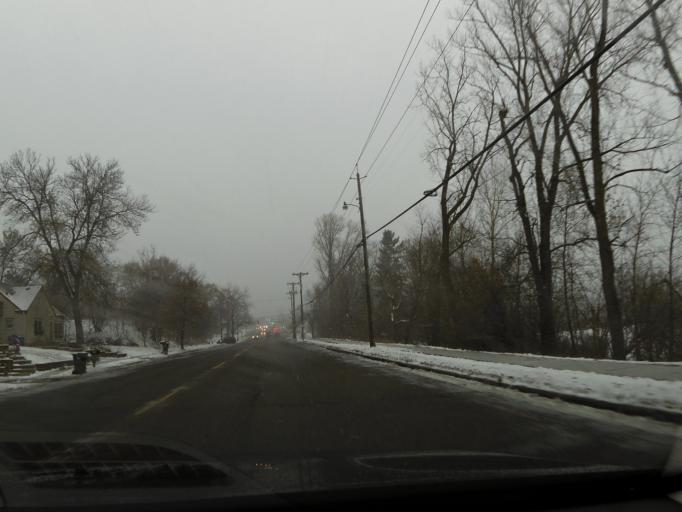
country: US
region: Minnesota
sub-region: Ramsey County
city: Maplewood
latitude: 44.9476
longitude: -93.0252
